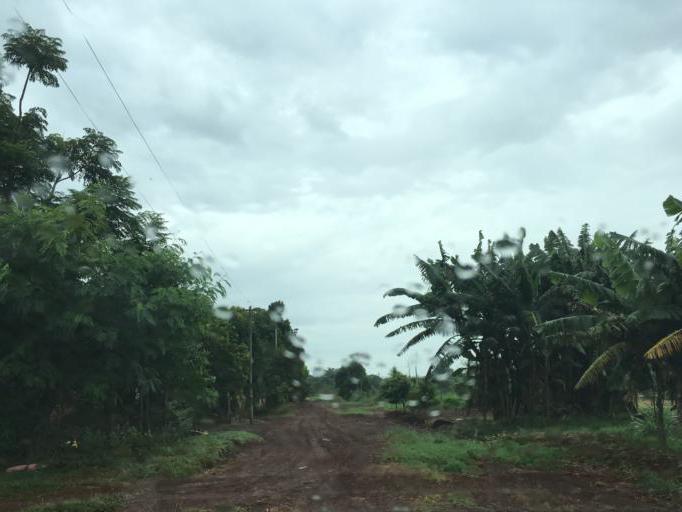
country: PY
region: Alto Parana
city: Ciudad del Este
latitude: -25.4350
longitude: -54.6539
